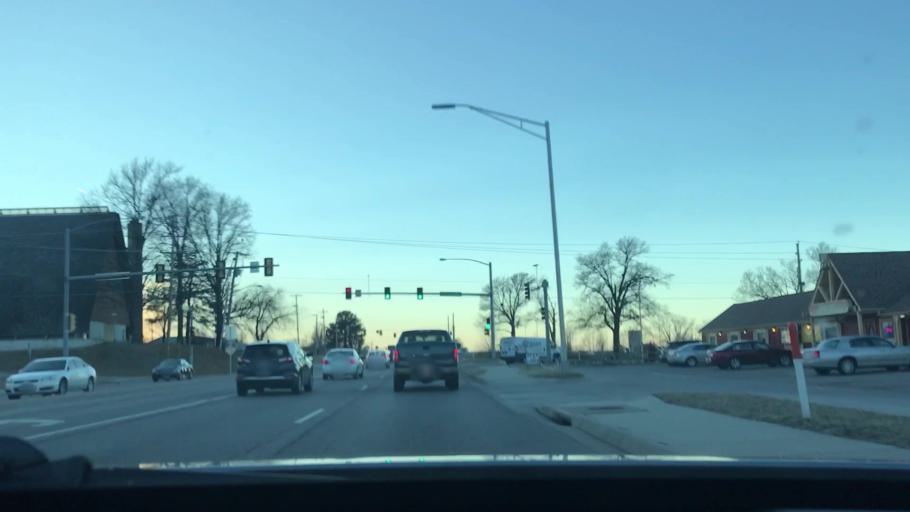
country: US
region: Kansas
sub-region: Wyandotte County
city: Edwardsville
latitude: 39.1165
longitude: -94.7971
